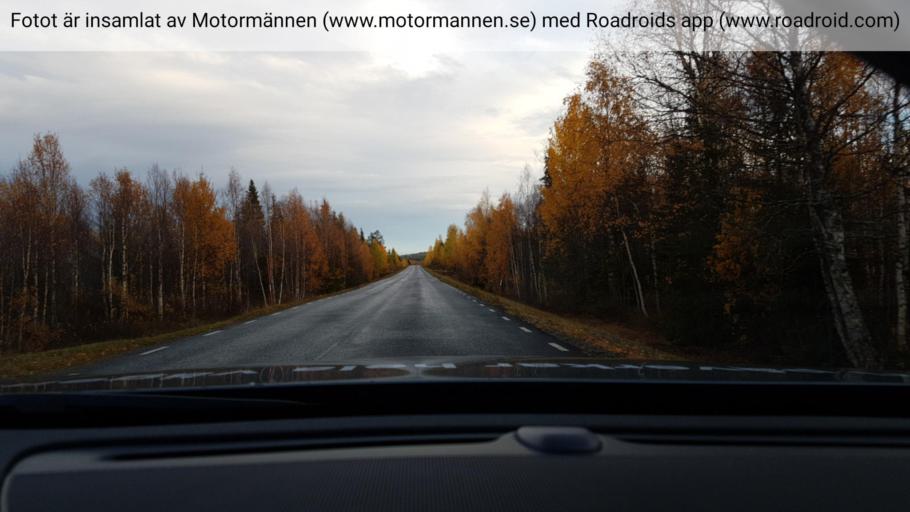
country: SE
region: Norrbotten
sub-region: Overkalix Kommun
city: OEverkalix
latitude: 66.9200
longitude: 22.7518
